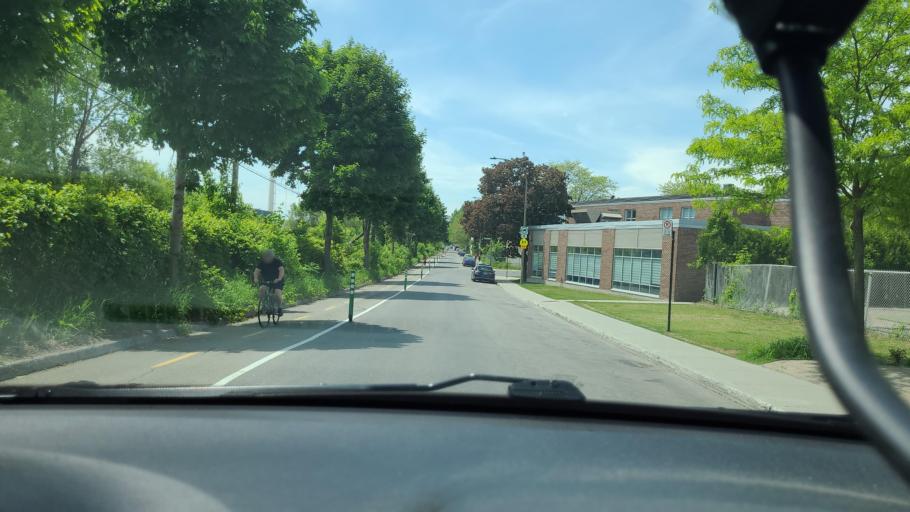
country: CA
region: Quebec
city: Saint-Raymond
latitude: 45.4619
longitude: -73.6264
